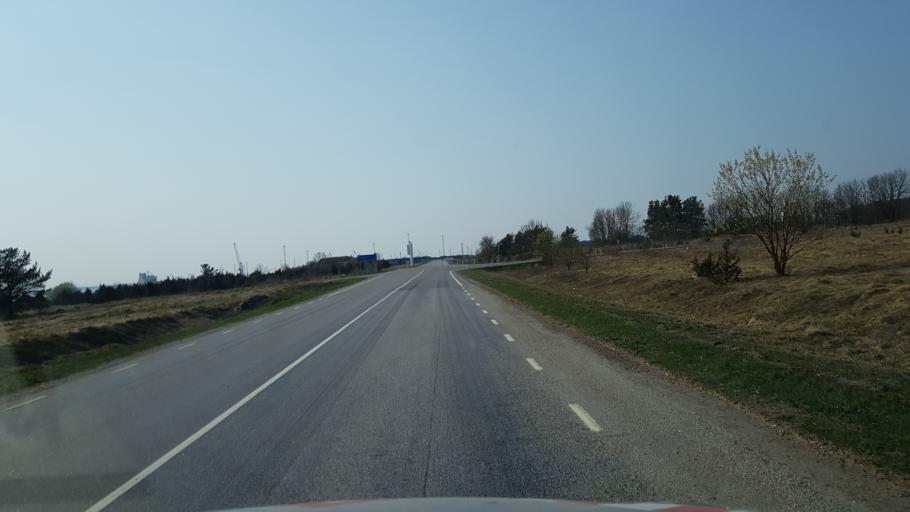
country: EE
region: Harju
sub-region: Paldiski linn
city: Paldiski
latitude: 59.3307
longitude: 24.1038
